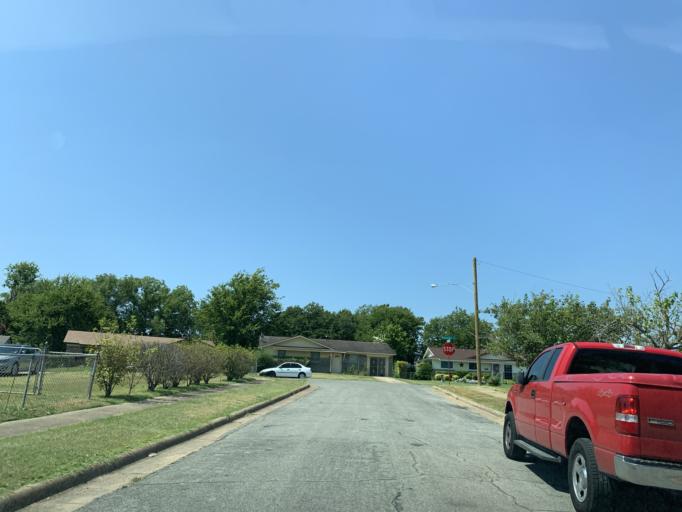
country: US
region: Texas
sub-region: Dallas County
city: Hutchins
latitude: 32.6767
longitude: -96.7515
